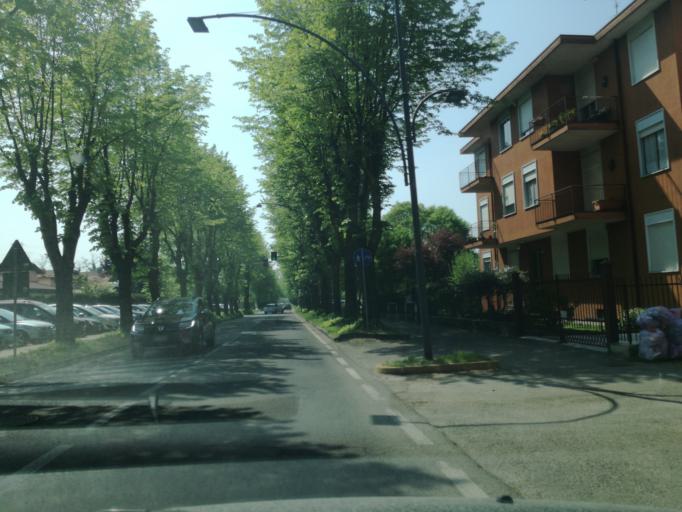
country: IT
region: Lombardy
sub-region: Provincia di Lecco
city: Paderno d'Adda
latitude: 45.6770
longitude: 9.4401
